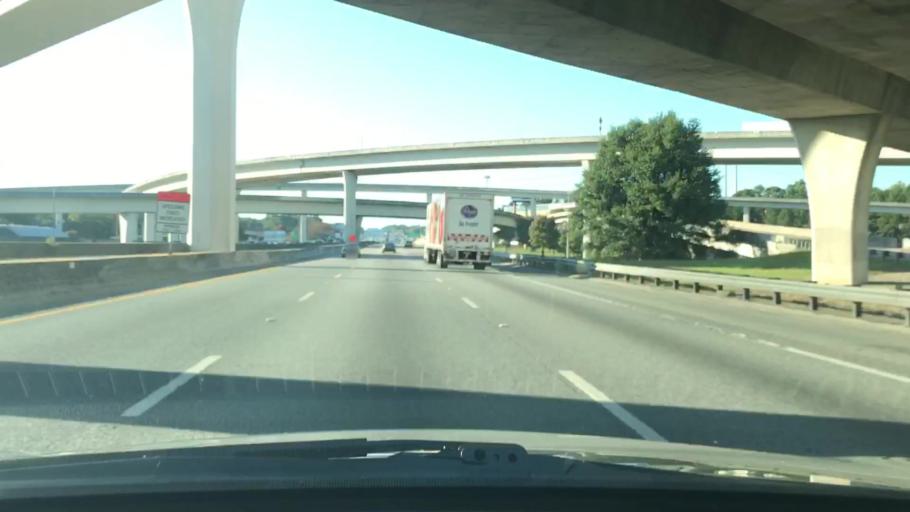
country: US
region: Georgia
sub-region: DeKalb County
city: Doraville
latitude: 33.8913
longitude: -84.2582
